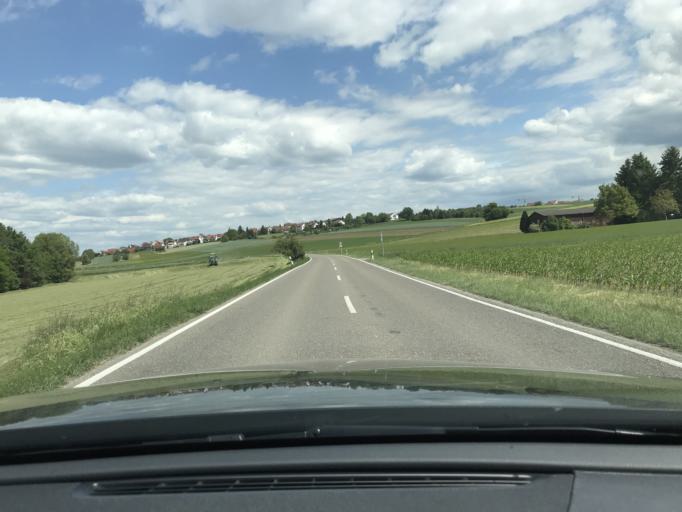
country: DE
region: Baden-Wuerttemberg
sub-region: Regierungsbezirk Stuttgart
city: Schwaikheim
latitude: 48.8724
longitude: 9.3346
